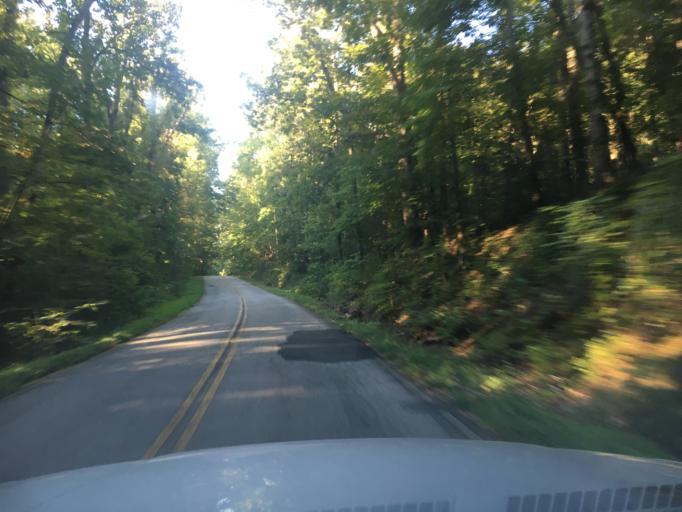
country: US
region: South Carolina
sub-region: Spartanburg County
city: Woodruff
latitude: 34.6713
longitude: -81.9635
